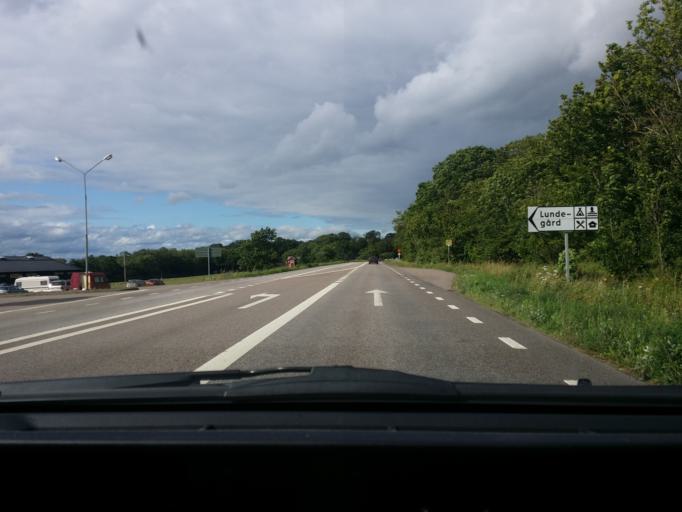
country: SE
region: Kalmar
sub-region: Borgholms Kommun
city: Borgholm
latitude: 56.9051
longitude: 16.7343
